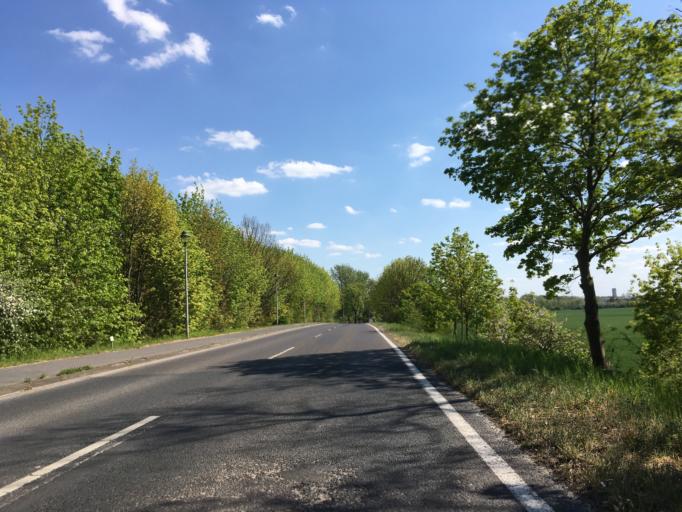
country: DE
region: Brandenburg
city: Werneuchen
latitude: 52.6178
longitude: 13.6758
